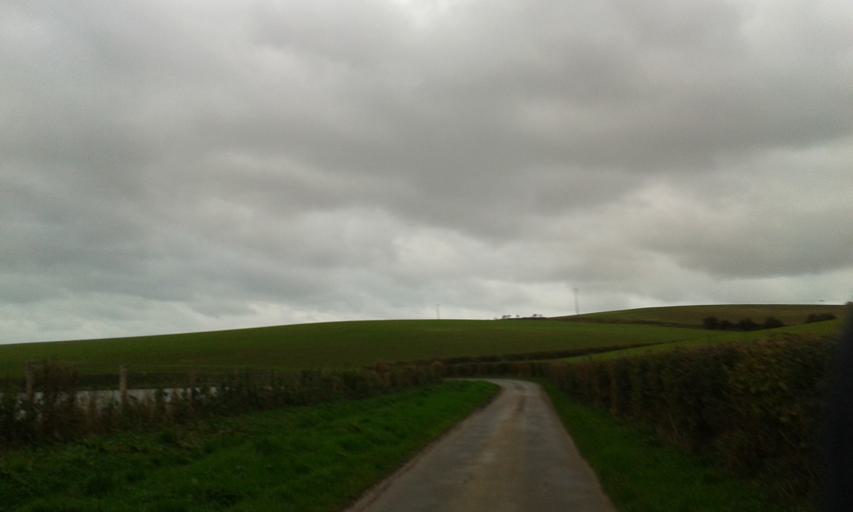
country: FR
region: Nord-Pas-de-Calais
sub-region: Departement du Pas-de-Calais
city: Ferques
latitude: 50.8733
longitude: 1.7358
